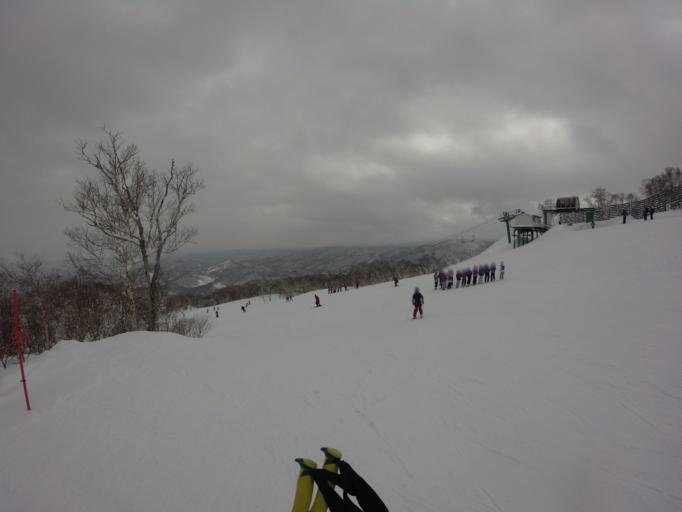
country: JP
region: Hokkaido
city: Sapporo
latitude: 43.0747
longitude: 141.1973
